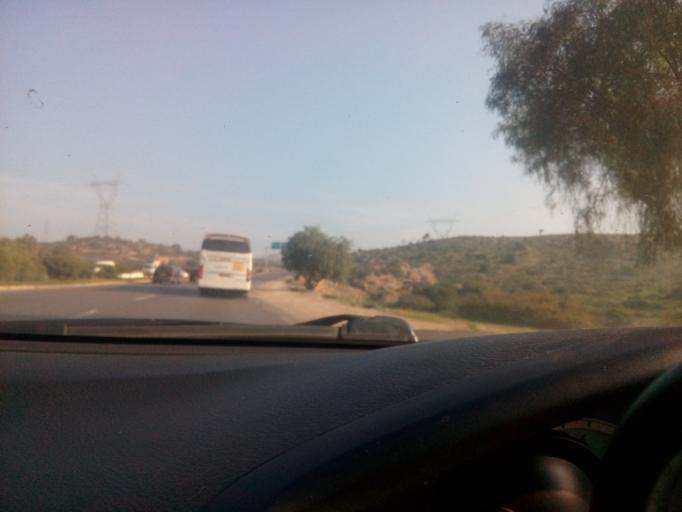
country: DZ
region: Oran
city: Es Senia
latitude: 35.6342
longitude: -0.7109
